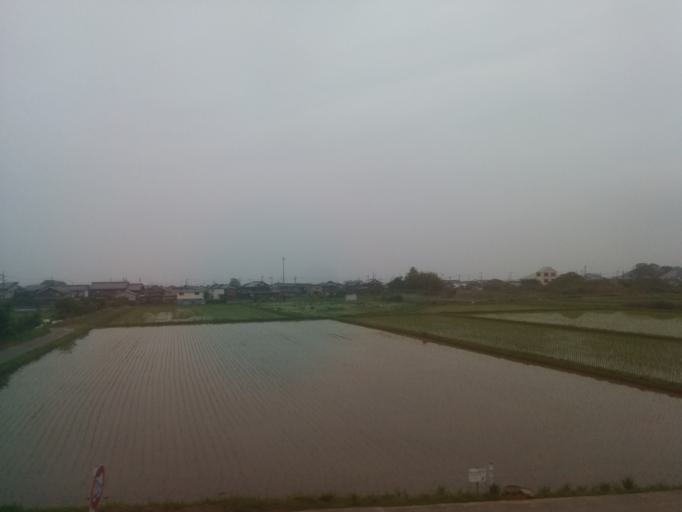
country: JP
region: Shiga Prefecture
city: Hikone
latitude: 35.2338
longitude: 136.2346
